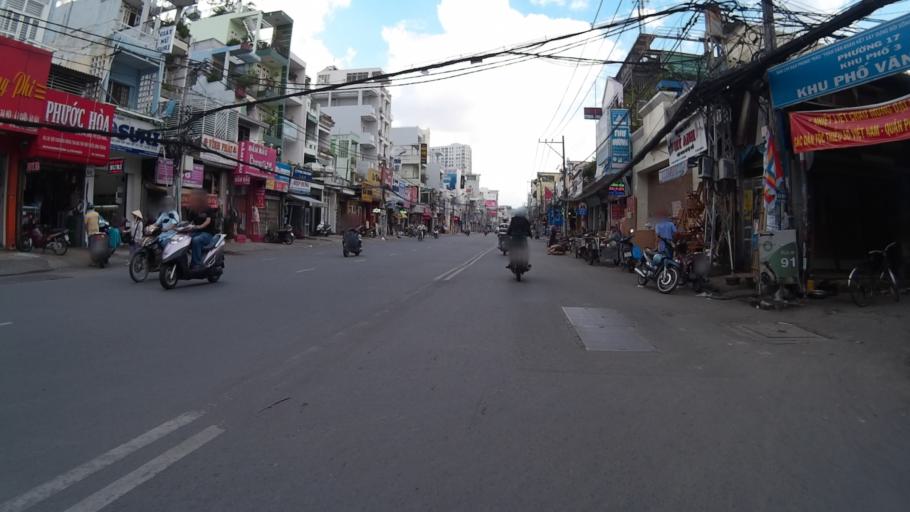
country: VN
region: Ho Chi Minh City
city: Quan Phu Nhuan
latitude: 10.7942
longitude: 106.6839
